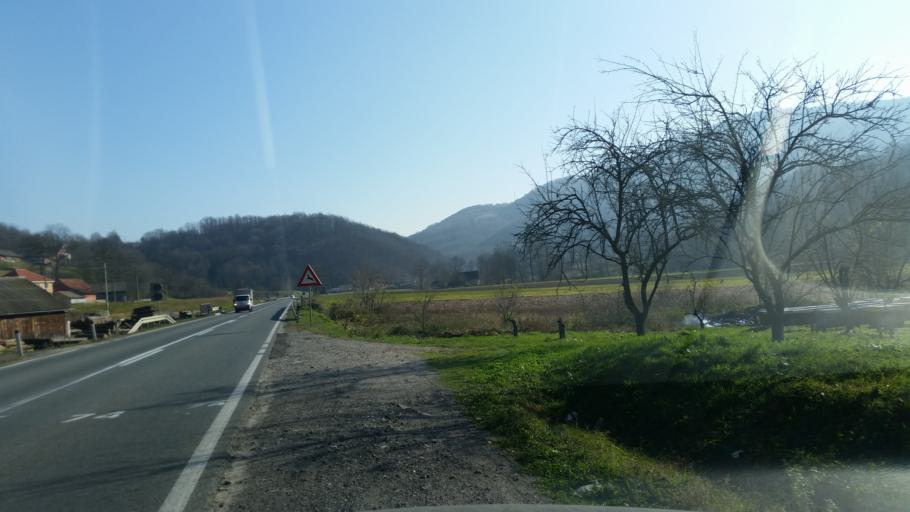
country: RS
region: Central Serbia
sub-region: Kolubarski Okrug
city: Ljig
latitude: 44.2029
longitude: 20.2477
